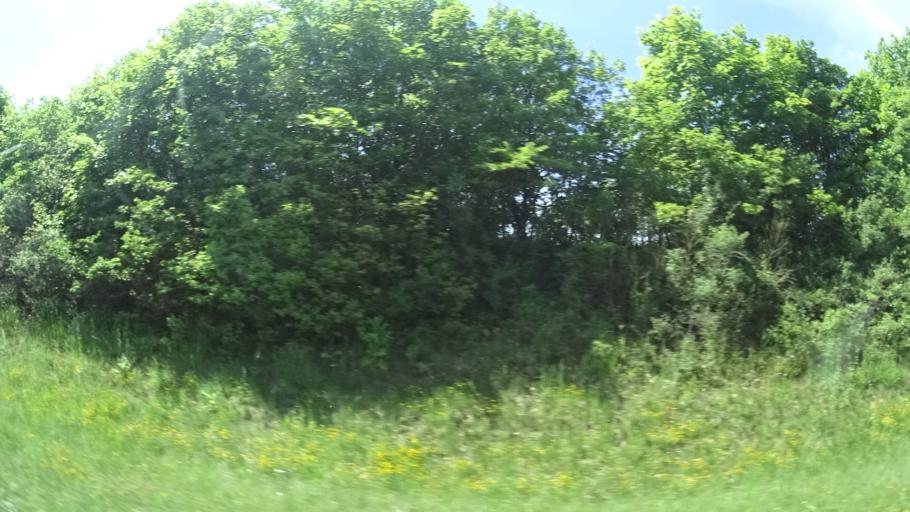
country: DE
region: Bavaria
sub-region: Regierungsbezirk Unterfranken
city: Oerlenbach
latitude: 50.1656
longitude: 10.1484
